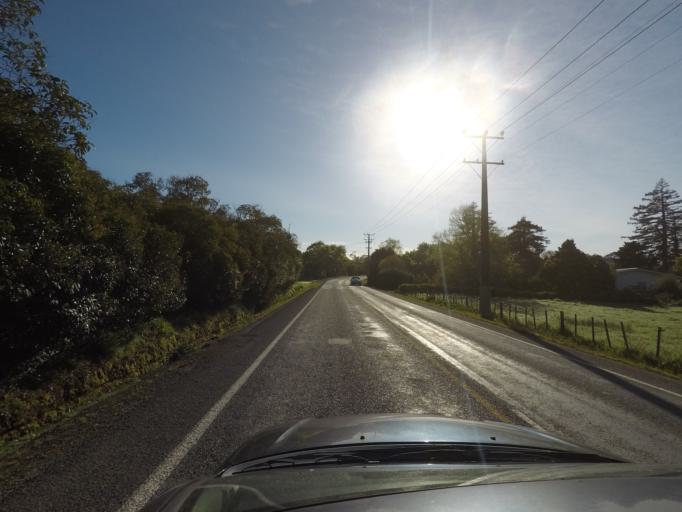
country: NZ
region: Auckland
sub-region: Auckland
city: Red Hill
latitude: -36.9989
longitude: 174.9676
